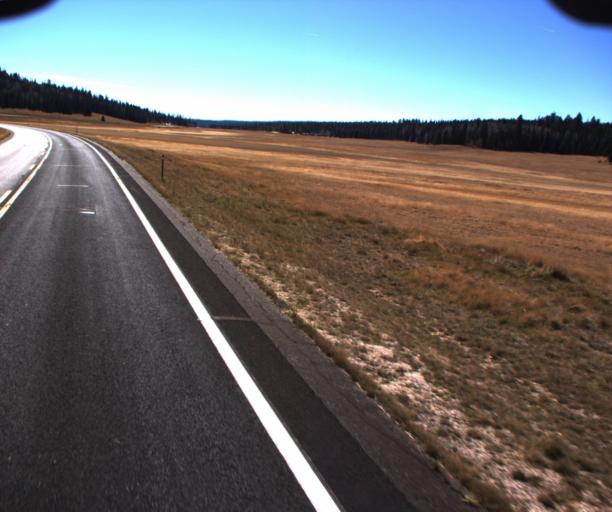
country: US
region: Arizona
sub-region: Coconino County
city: Grand Canyon
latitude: 36.4262
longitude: -112.1315
